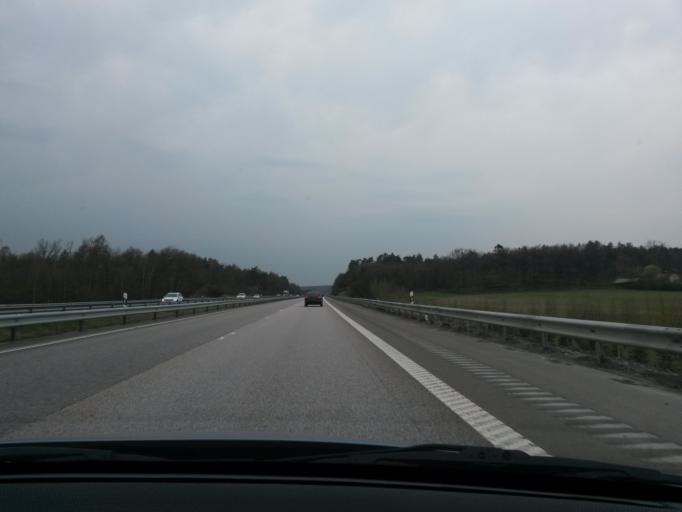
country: SE
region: Halland
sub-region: Varbergs Kommun
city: Veddige
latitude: 57.2086
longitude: 12.2429
